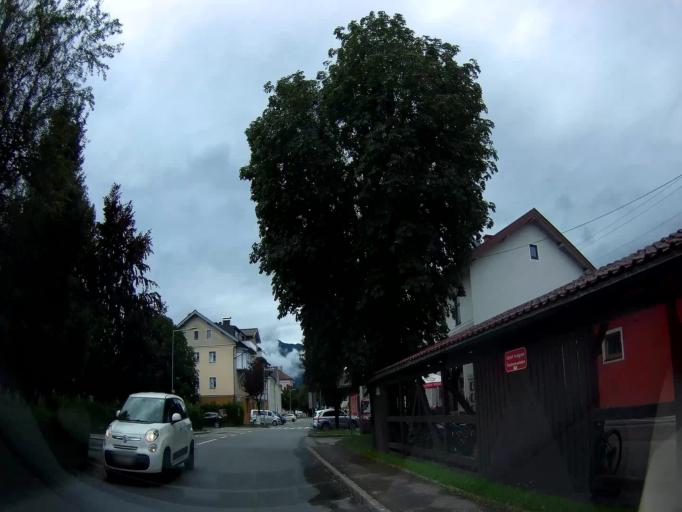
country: AT
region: Salzburg
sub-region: Politischer Bezirk Zell am See
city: Saalfelden am Steinernen Meer
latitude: 47.4273
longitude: 12.8303
